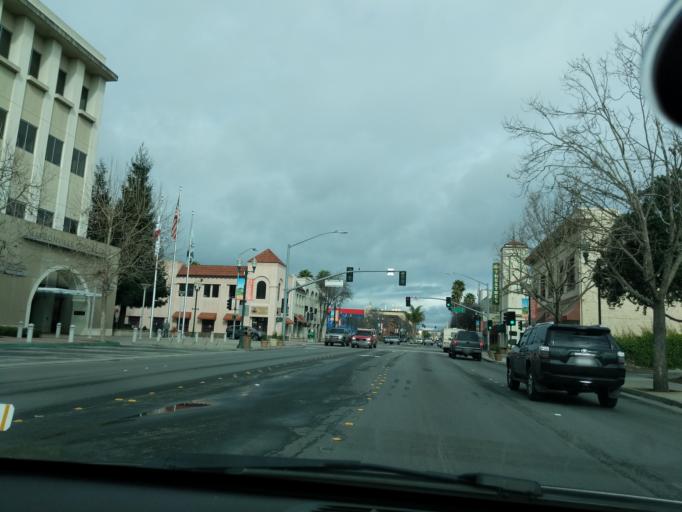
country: US
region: California
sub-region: Santa Cruz County
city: Watsonville
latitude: 36.9088
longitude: -121.7552
